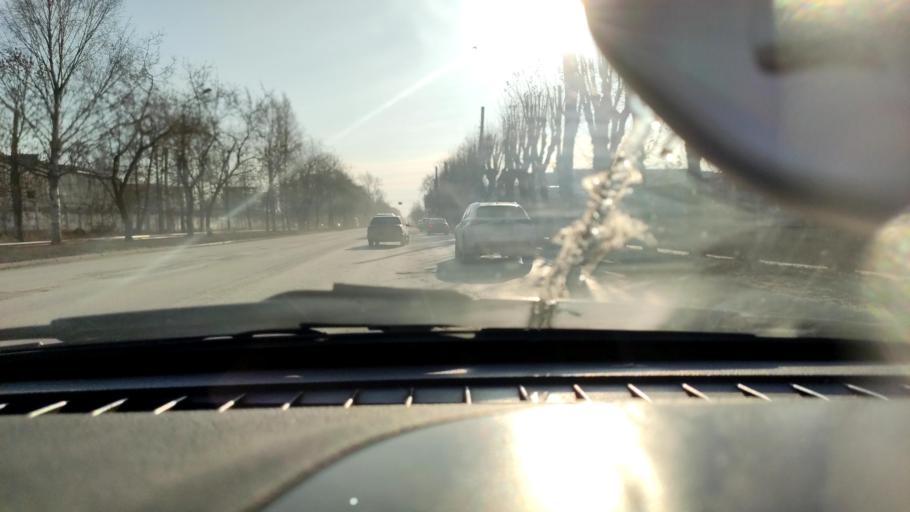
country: RU
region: Perm
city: Perm
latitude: 57.9709
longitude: 56.2459
